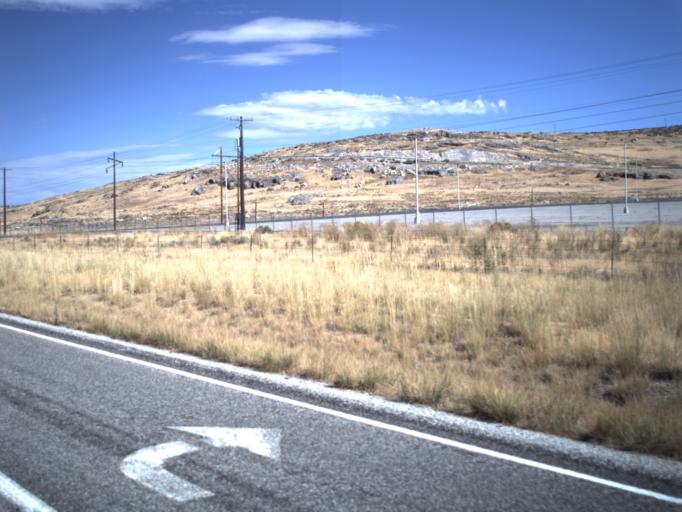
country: US
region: Utah
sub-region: Box Elder County
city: Tremonton
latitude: 41.6379
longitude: -112.4250
